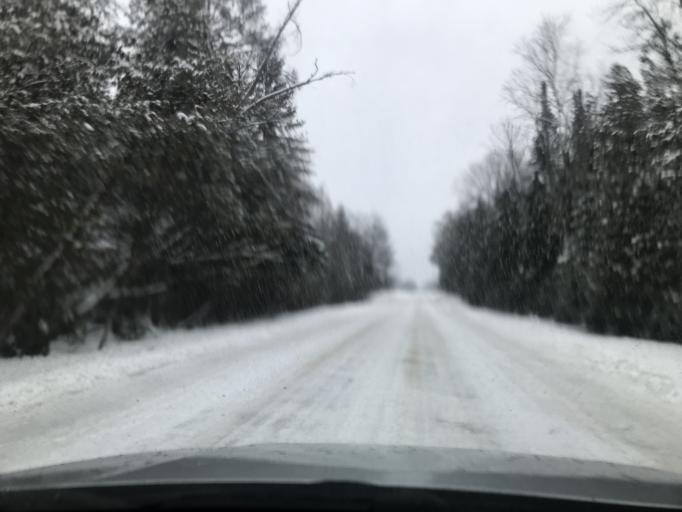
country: US
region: Wisconsin
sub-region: Marinette County
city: Peshtigo
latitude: 45.3812
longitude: -87.9344
